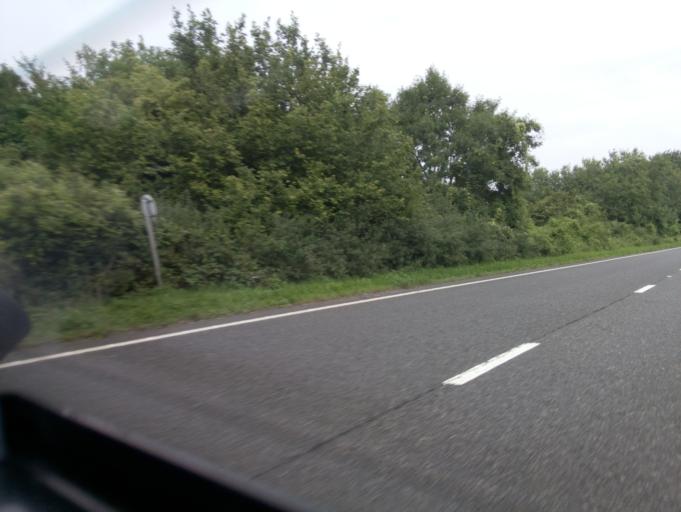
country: GB
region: England
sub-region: Gloucestershire
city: Coates
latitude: 51.7705
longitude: -2.0228
